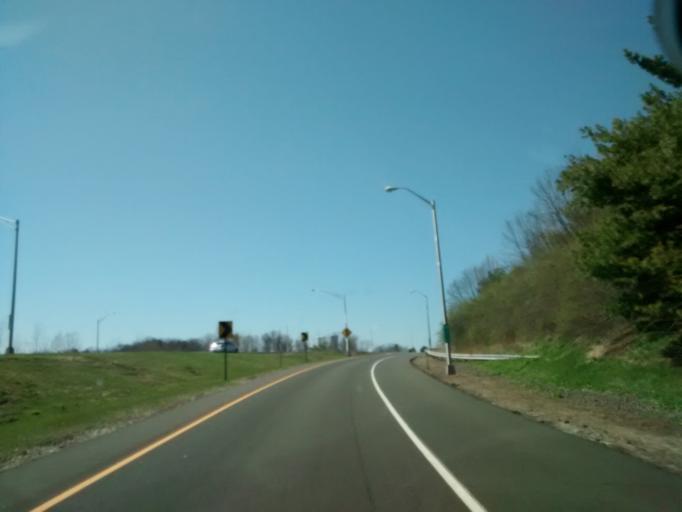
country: US
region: Connecticut
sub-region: Hartford County
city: East Hartford
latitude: 41.7911
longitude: -72.5685
